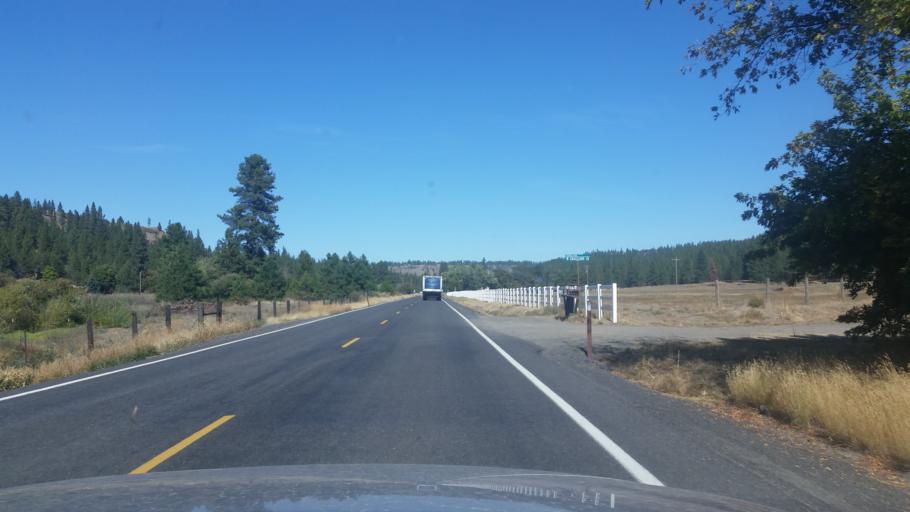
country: US
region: Washington
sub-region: Spokane County
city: Spokane
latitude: 47.5905
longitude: -117.4508
